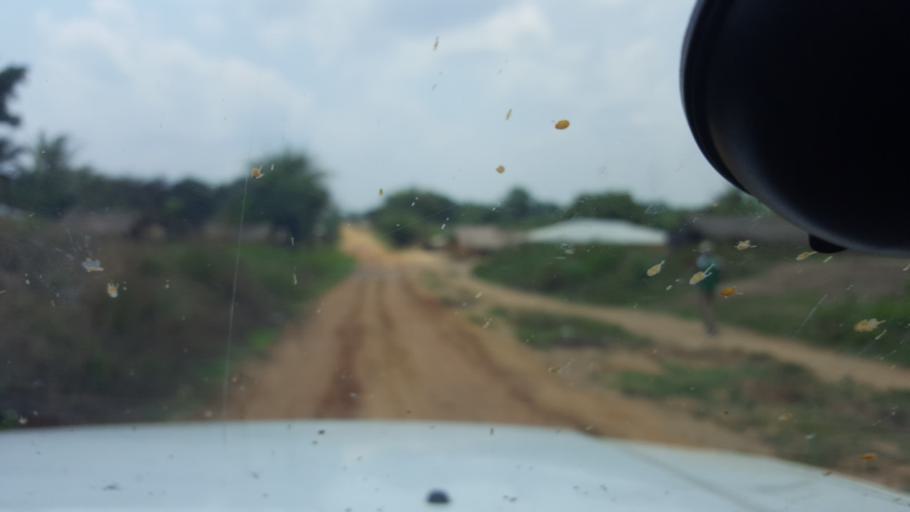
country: CD
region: Bandundu
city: Mushie
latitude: -3.7457
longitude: 16.6505
